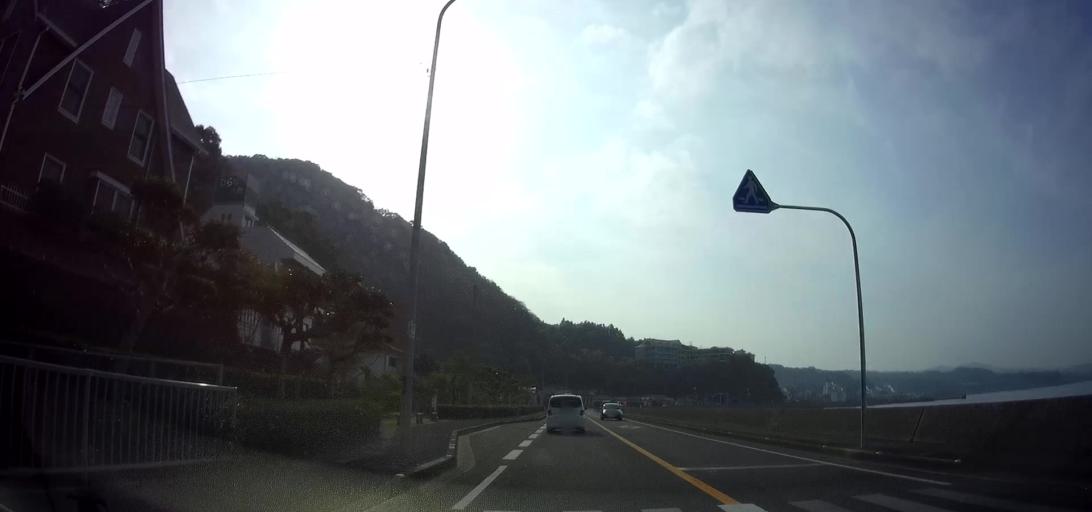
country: JP
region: Nagasaki
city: Shimabara
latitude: 32.7402
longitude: 130.2097
